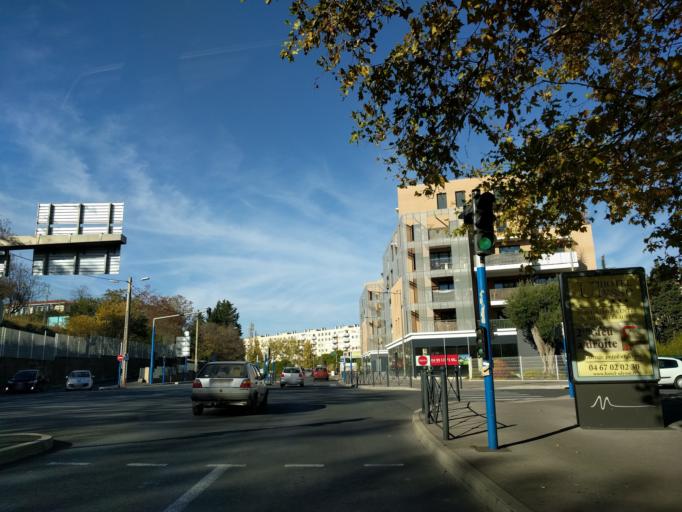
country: FR
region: Languedoc-Roussillon
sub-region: Departement de l'Herault
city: Montpellier
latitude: 43.6120
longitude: 3.8897
